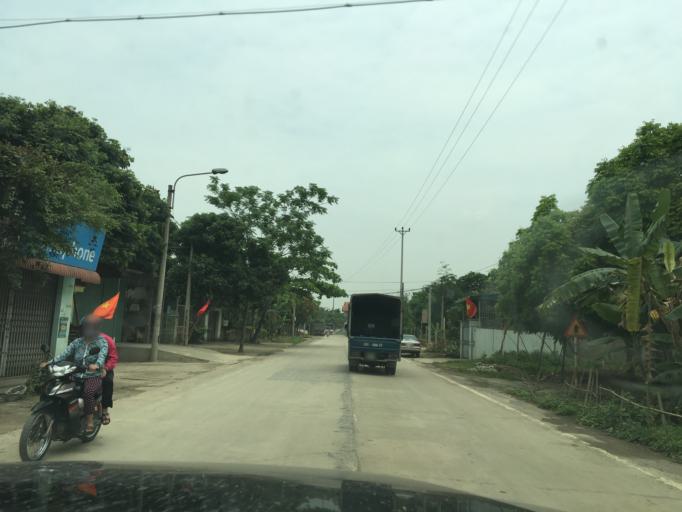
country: VN
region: Ninh Binh
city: Thi Tran Tam Diep
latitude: 20.1831
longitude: 105.8911
